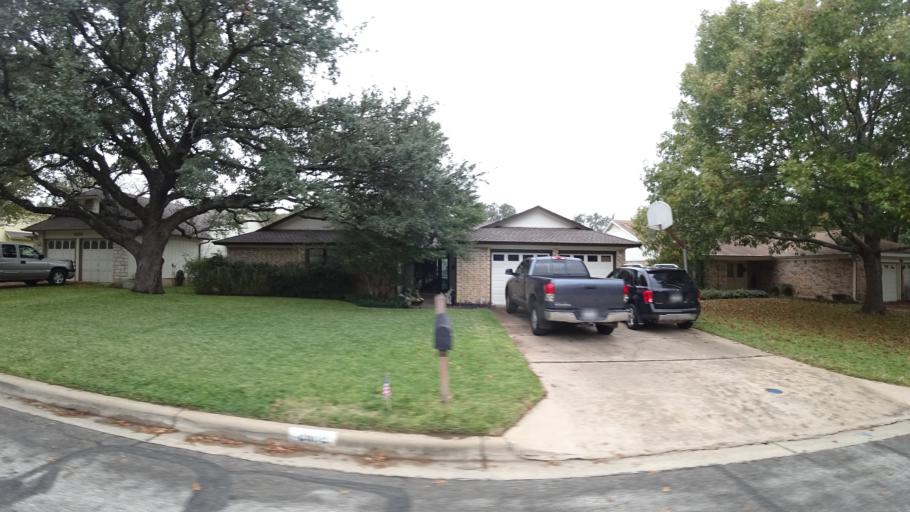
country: US
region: Texas
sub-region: Williamson County
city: Round Rock
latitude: 30.4856
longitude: -97.7014
